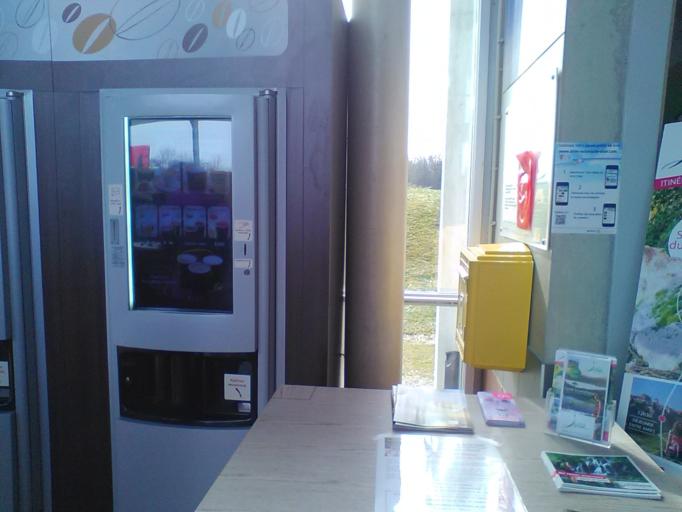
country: FR
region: Franche-Comte
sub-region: Departement du Jura
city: Bletterans
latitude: 46.7732
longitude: 5.5210
